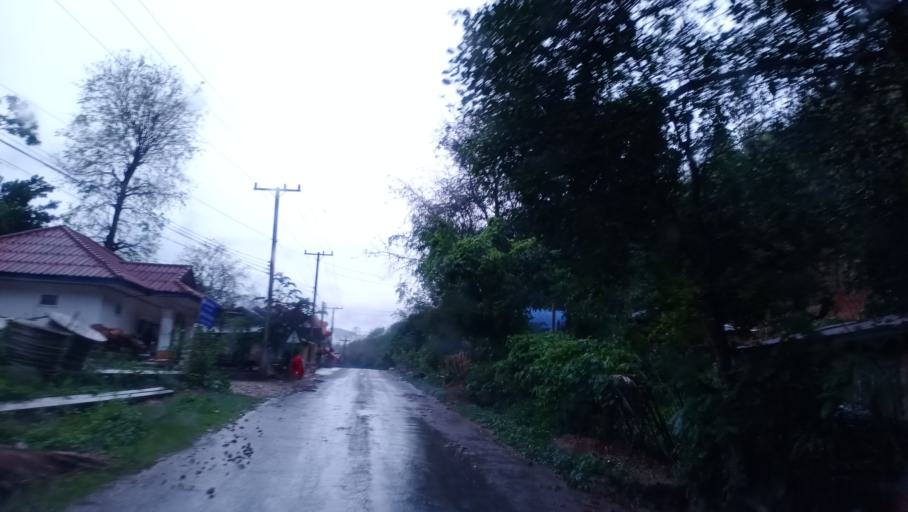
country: LA
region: Phongsali
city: Khoa
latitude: 21.0714
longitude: 102.4936
